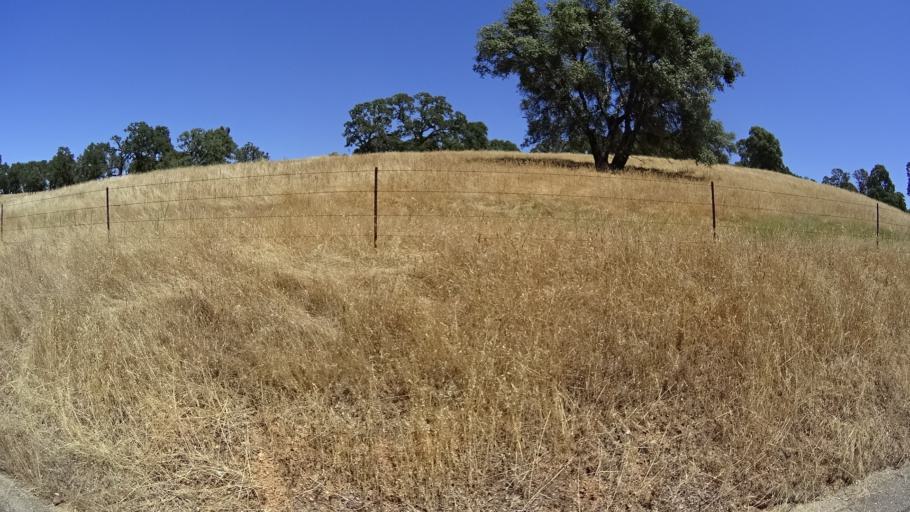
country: US
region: California
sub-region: Calaveras County
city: San Andreas
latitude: 38.1033
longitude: -120.6613
